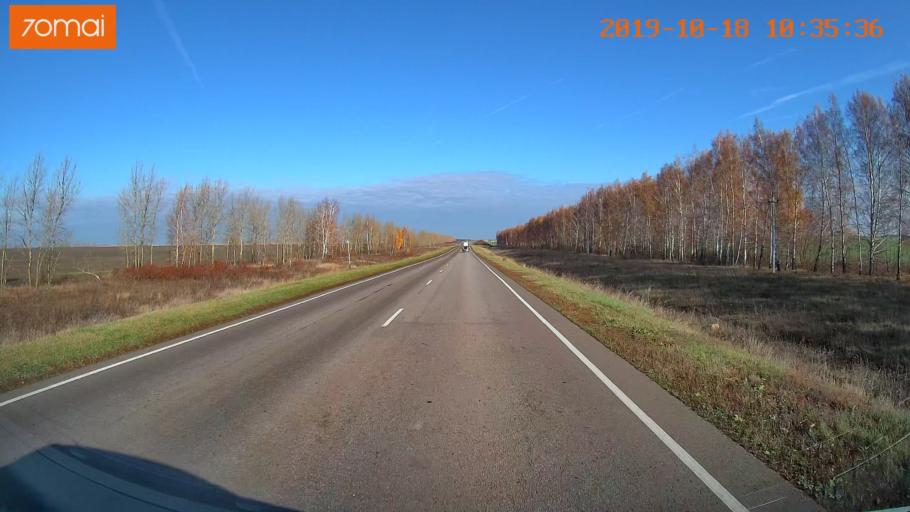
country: RU
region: Tula
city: Kurkino
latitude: 53.5355
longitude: 38.6206
